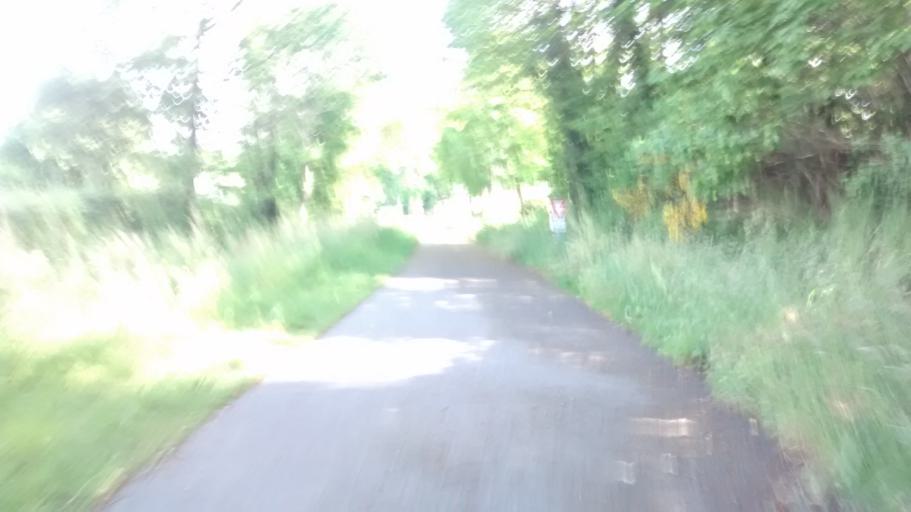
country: FR
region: Brittany
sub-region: Departement du Morbihan
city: Pleucadeuc
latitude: 47.7749
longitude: -2.3981
